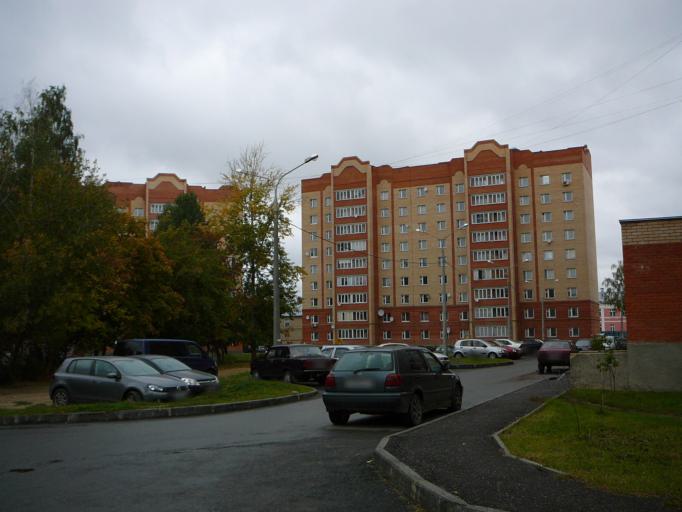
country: RU
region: Moskovskaya
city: Yegor'yevsk
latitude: 55.3897
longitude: 39.0290
